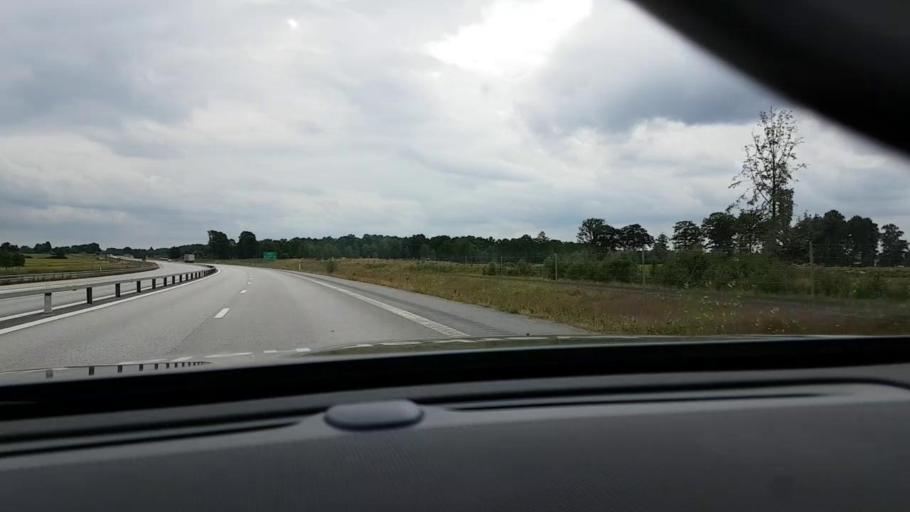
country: SE
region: Skane
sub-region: Horby Kommun
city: Hoerby
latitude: 55.8998
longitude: 13.7263
